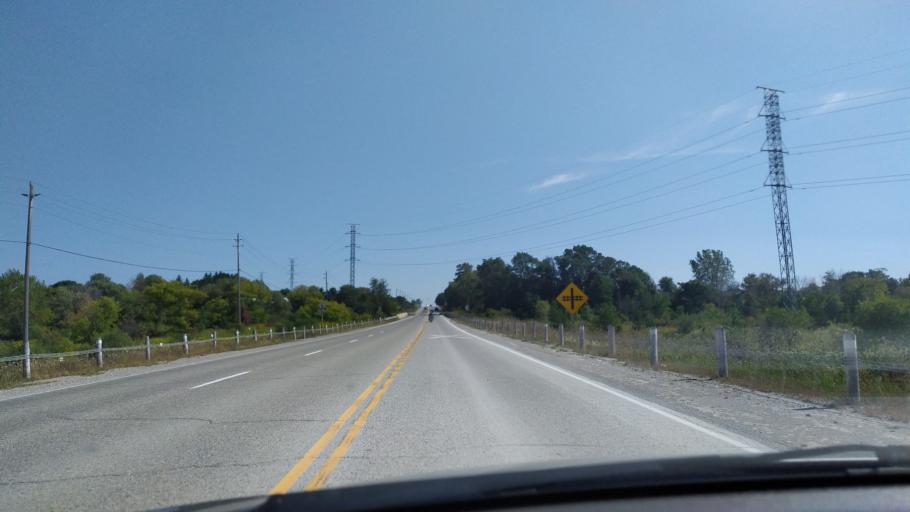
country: CA
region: Ontario
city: Ingersoll
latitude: 43.0703
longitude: -80.8513
